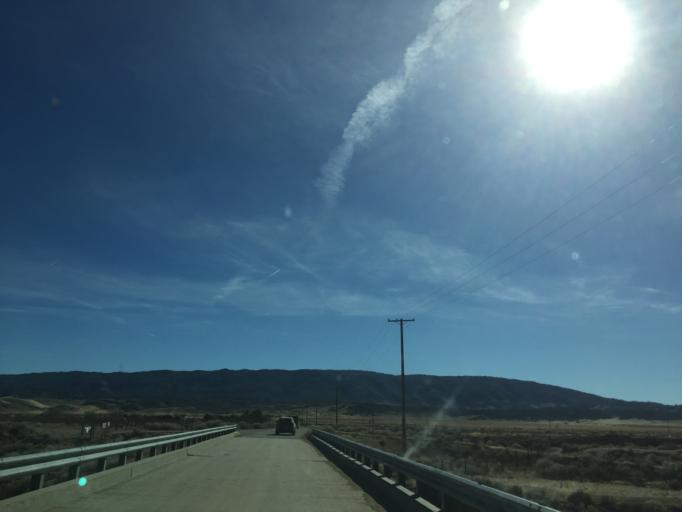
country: US
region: California
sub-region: Kern County
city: Lebec
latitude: 34.8082
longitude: -118.6611
